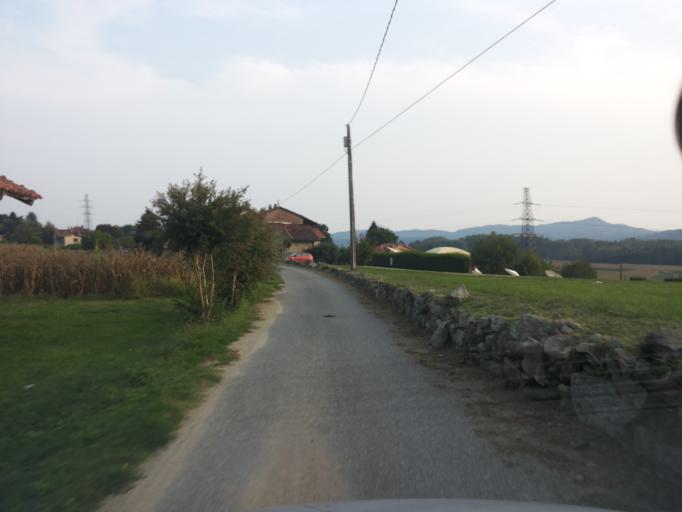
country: IT
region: Piedmont
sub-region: Provincia di Torino
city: Piverone
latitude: 45.4353
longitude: 8.0235
